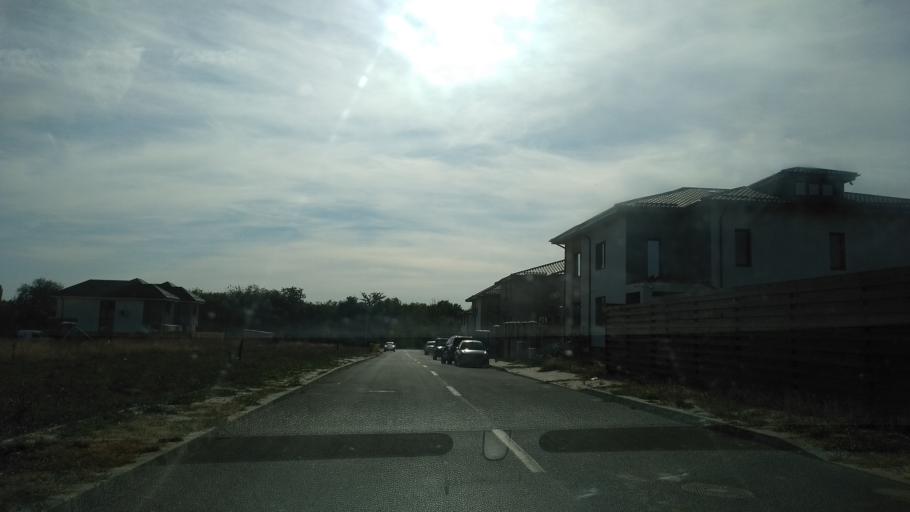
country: RO
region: Ilfov
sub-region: Comuna Chitila
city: Chitila
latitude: 44.5134
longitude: 25.9864
